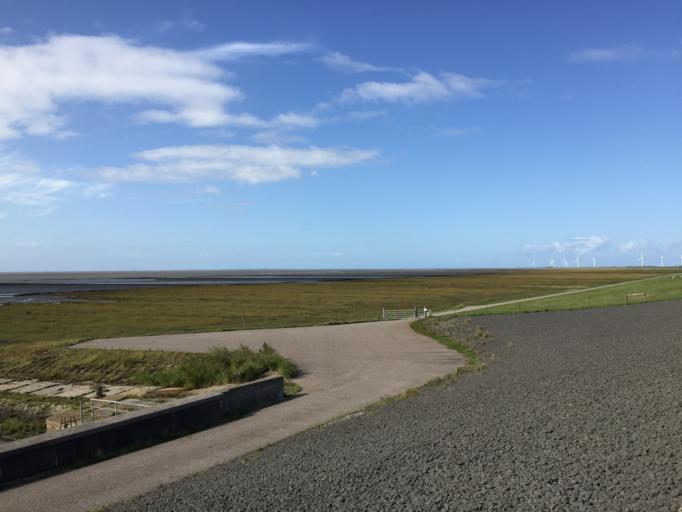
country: DE
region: Schleswig-Holstein
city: Emmelsbull-Horsbull
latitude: 54.7966
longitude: 8.6600
